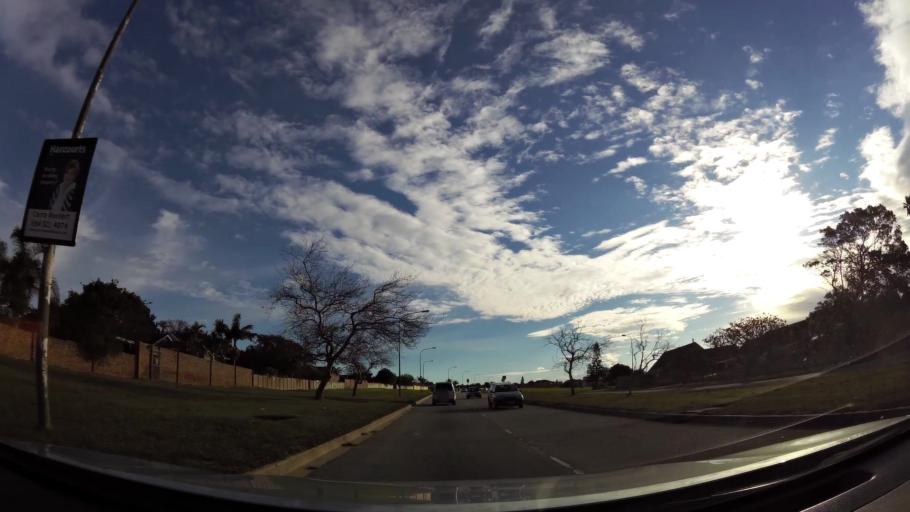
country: ZA
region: Eastern Cape
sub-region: Nelson Mandela Bay Metropolitan Municipality
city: Port Elizabeth
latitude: -33.9599
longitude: 25.4848
